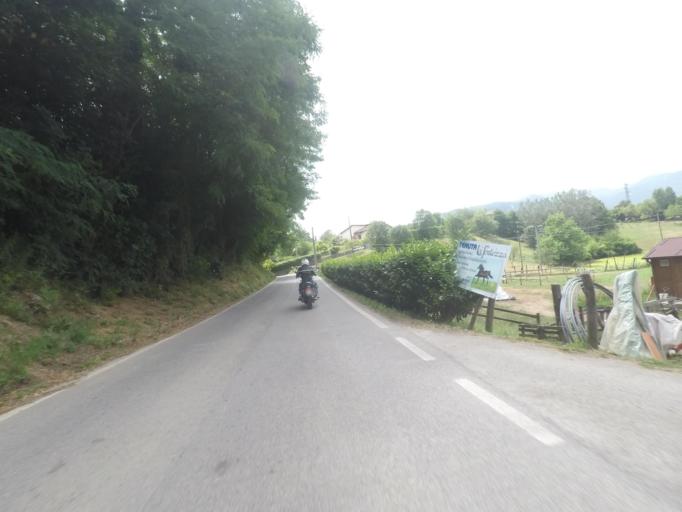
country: IT
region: Tuscany
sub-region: Provincia di Lucca
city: Castelnuovo di Garfagnana
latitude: 44.1100
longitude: 10.3947
